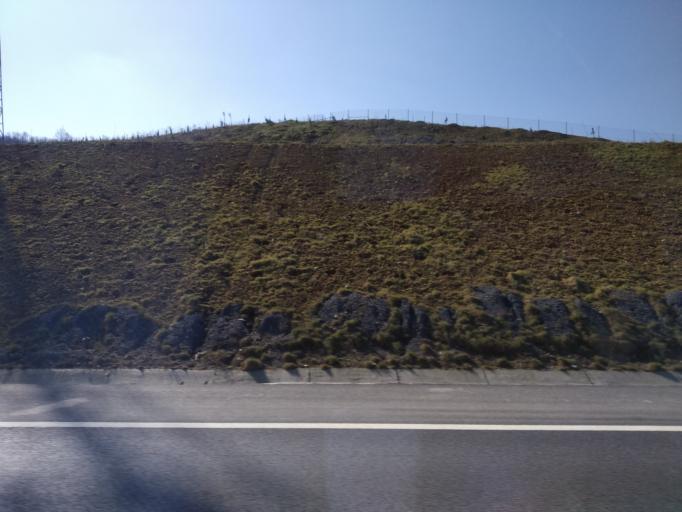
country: TR
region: Istanbul
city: Mahmut Sevket Pasa
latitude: 41.1618
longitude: 29.2583
